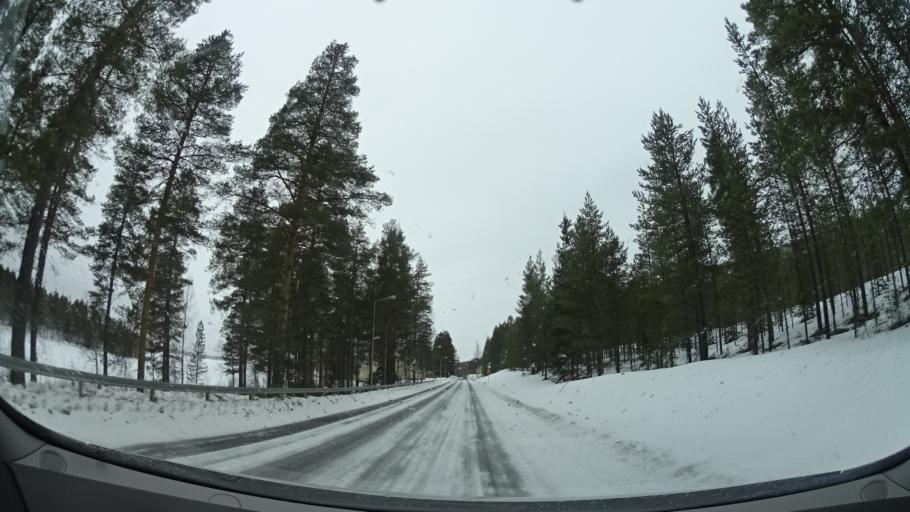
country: SE
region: Vaesterbotten
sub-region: Mala Kommun
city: Mala
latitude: 65.1702
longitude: 18.7638
